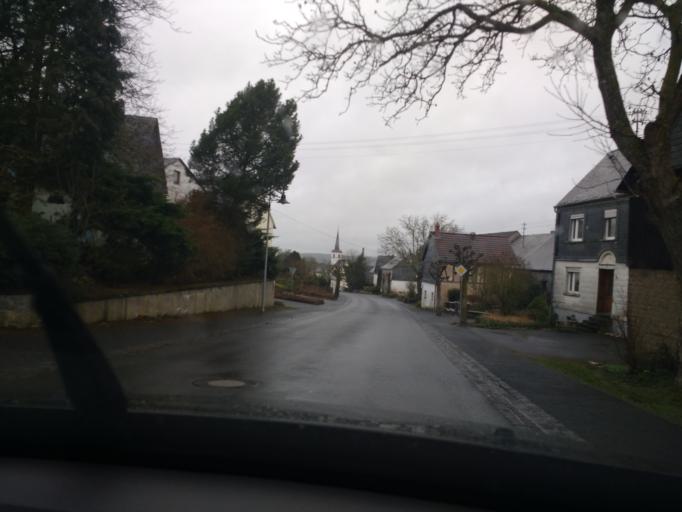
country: DE
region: Rheinland-Pfalz
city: Lotzbeuren
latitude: 49.9346
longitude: 7.2244
